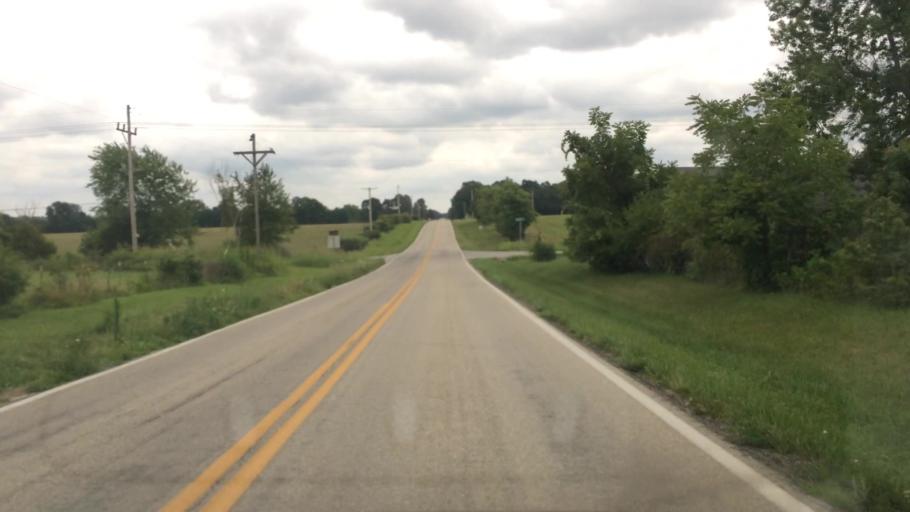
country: US
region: Missouri
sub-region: Greene County
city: Strafford
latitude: 37.3002
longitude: -93.1502
